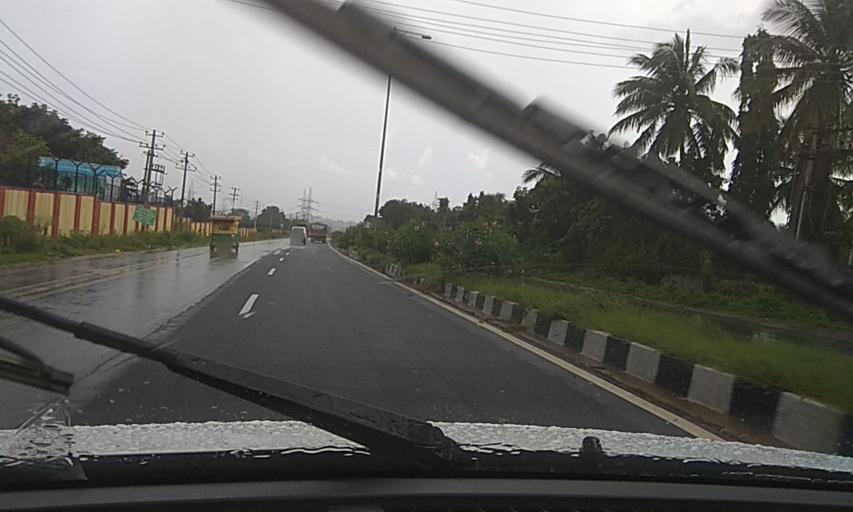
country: IN
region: Karnataka
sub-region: Mysore
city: Nanjangud
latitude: 12.2068
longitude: 76.6647
